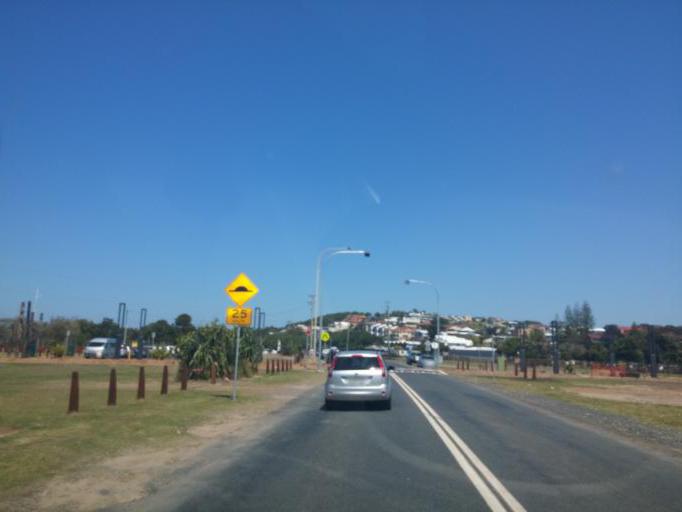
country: AU
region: New South Wales
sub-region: Coffs Harbour
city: Coffs Harbour
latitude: -30.3032
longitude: 153.1397
